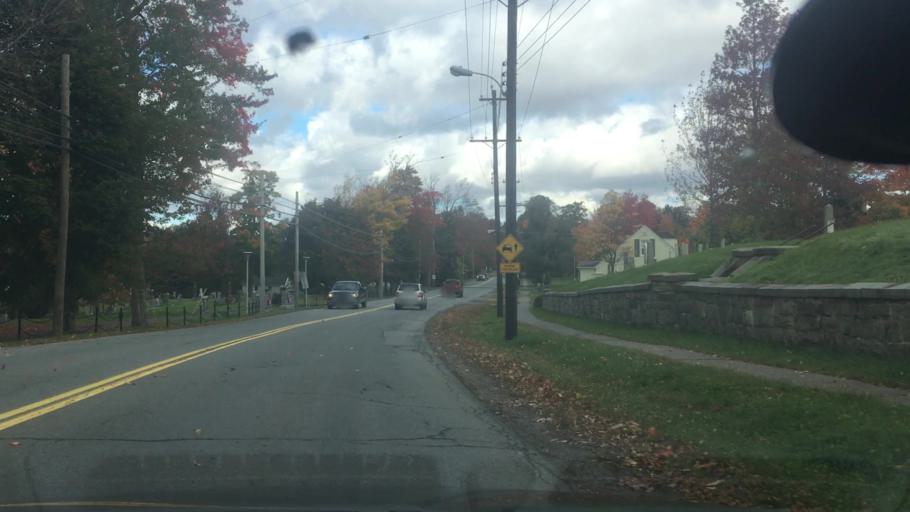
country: CA
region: Nova Scotia
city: Windsor
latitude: 44.9808
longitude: -64.1297
